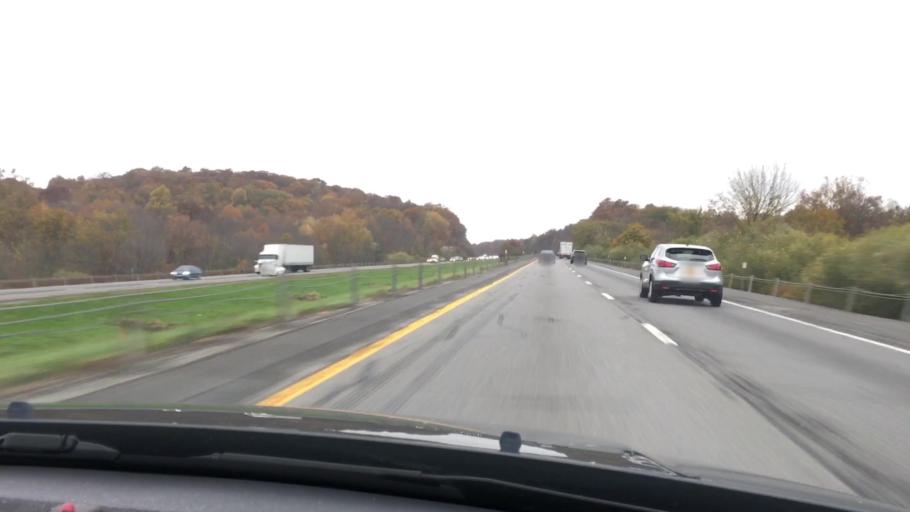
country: US
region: New York
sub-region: Putnam County
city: Brewster Hill
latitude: 41.4332
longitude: -73.6307
